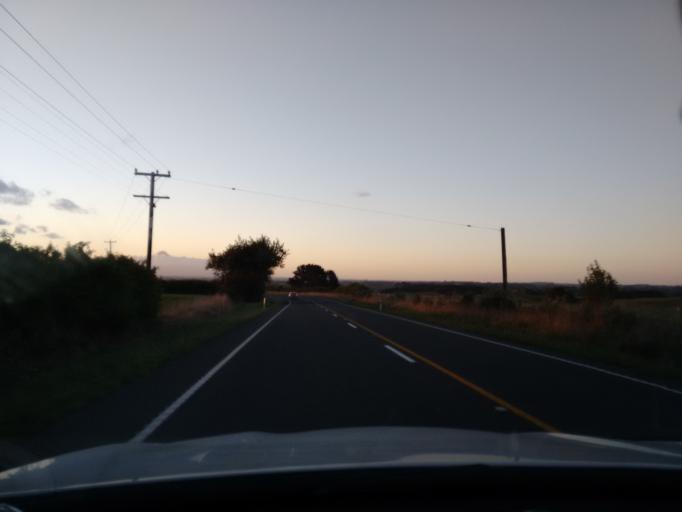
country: NZ
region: Taranaki
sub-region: South Taranaki District
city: Hawera
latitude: -39.6534
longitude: 174.3926
